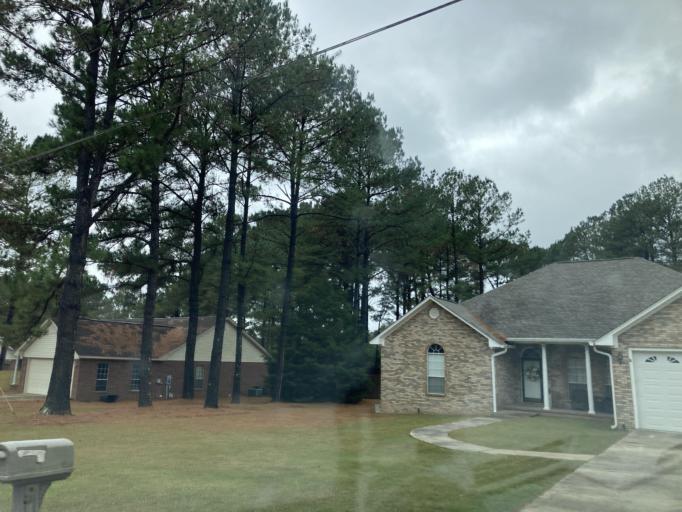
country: US
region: Mississippi
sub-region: Lamar County
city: West Hattiesburg
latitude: 31.2911
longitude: -89.4776
